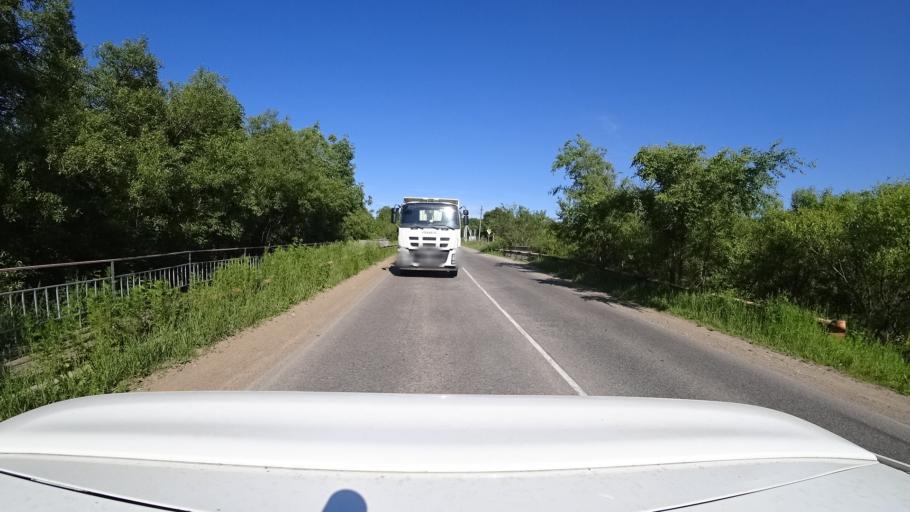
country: RU
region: Khabarovsk Krai
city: Topolevo
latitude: 48.5486
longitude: 135.1904
